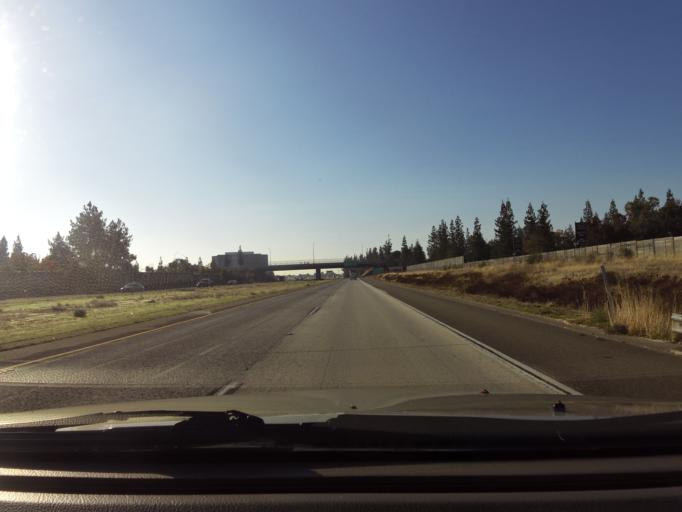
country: US
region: California
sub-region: Fresno County
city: Clovis
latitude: 36.8635
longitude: -119.7919
